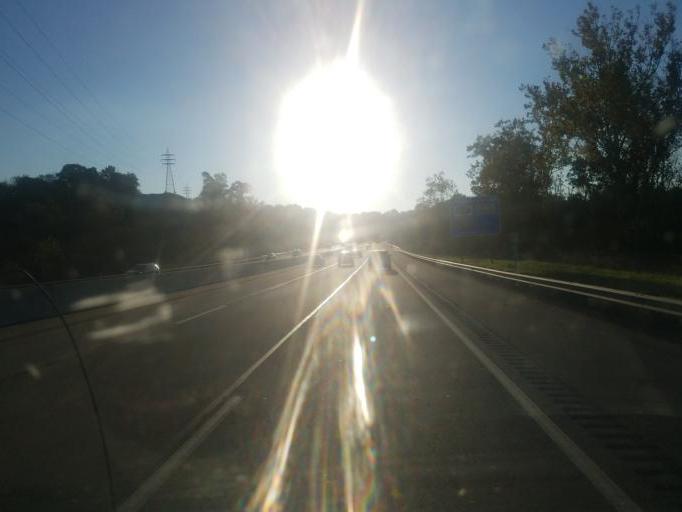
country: US
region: Pennsylvania
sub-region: Allegheny County
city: Oakmont
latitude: 40.5522
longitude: -79.8319
